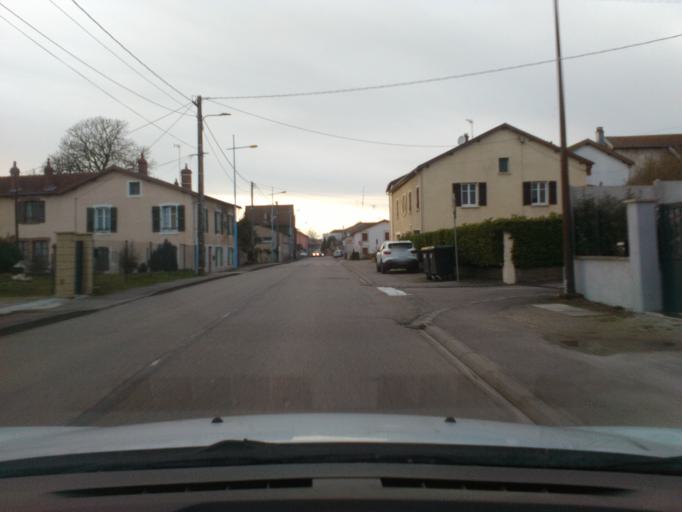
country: FR
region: Lorraine
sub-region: Departement des Vosges
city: Charmes
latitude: 48.3751
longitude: 6.3018
